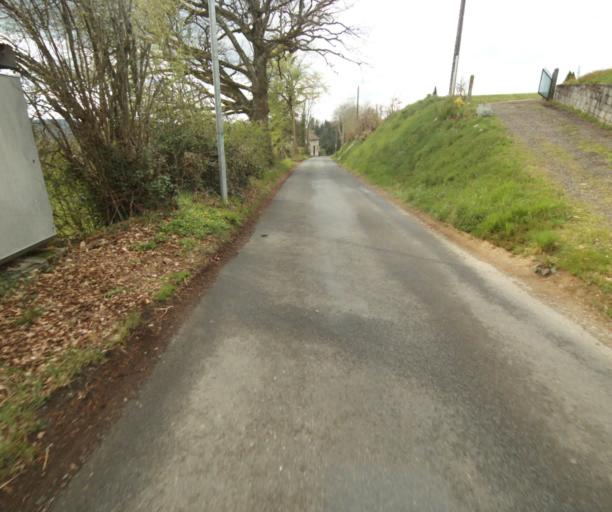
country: FR
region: Limousin
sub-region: Departement de la Correze
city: Tulle
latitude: 45.2745
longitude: 1.7512
